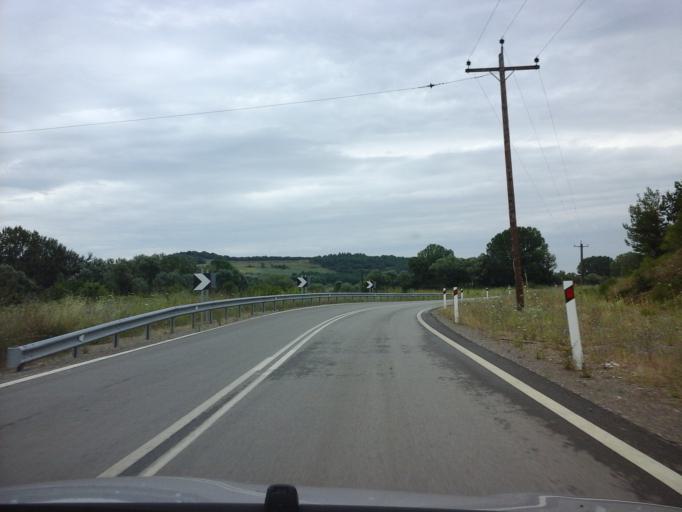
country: GR
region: East Macedonia and Thrace
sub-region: Nomos Evrou
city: Soufli
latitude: 41.1400
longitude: 26.2735
